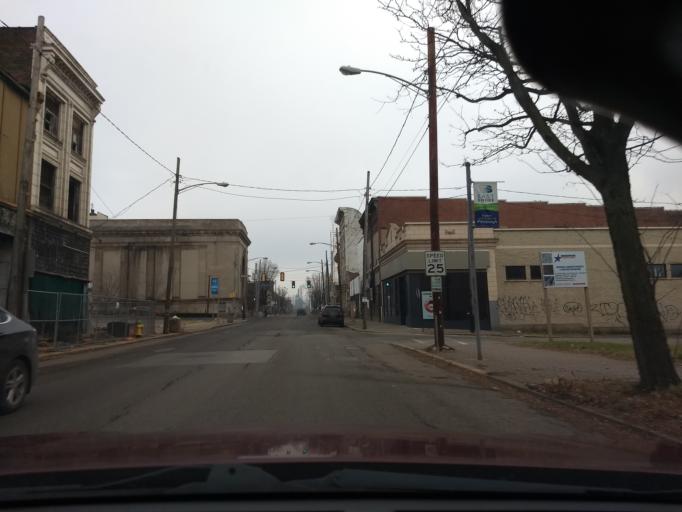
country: US
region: Pennsylvania
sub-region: Allegheny County
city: Braddock
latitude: 40.4017
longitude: -79.8664
